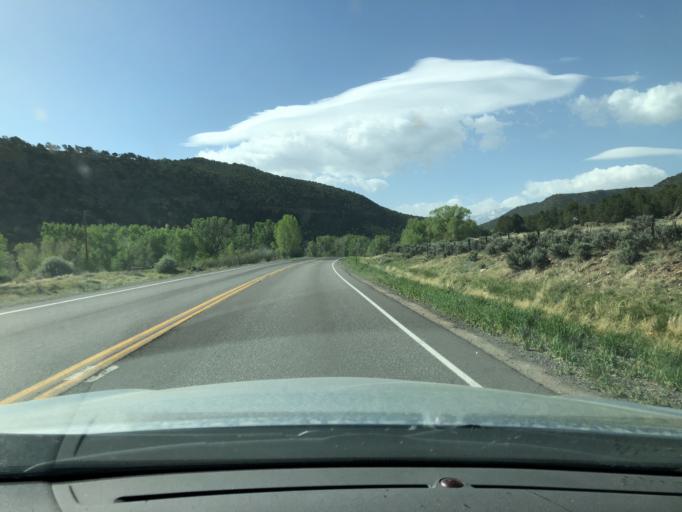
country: US
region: Colorado
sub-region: Montrose County
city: Montrose
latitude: 38.2869
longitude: -107.7657
